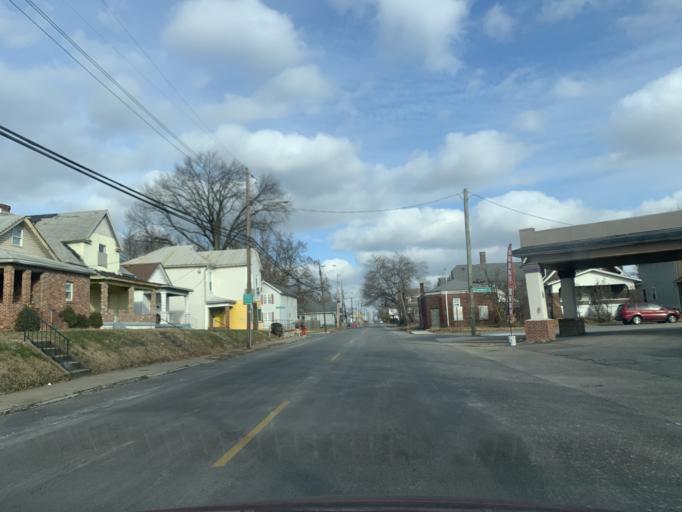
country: US
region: Kentucky
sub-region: Jefferson County
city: Louisville
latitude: 38.2414
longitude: -85.7958
